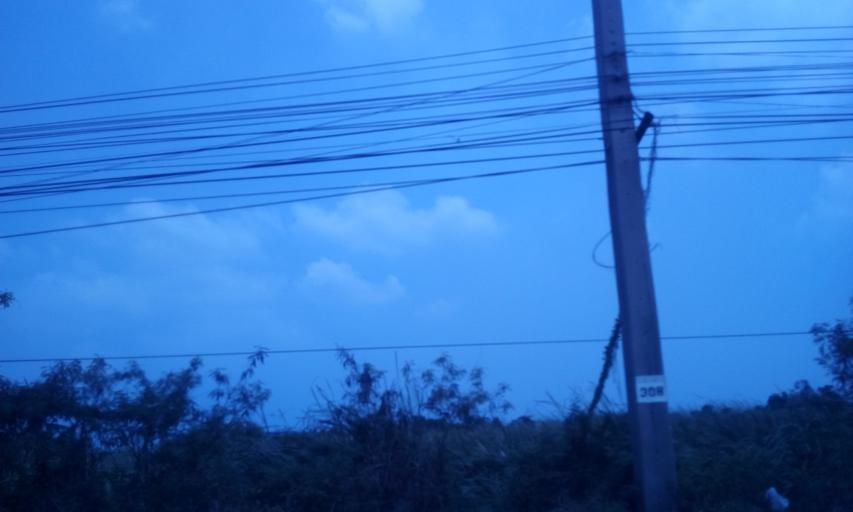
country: TH
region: Chachoengsao
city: Ban Pho
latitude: 13.6377
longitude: 101.1033
